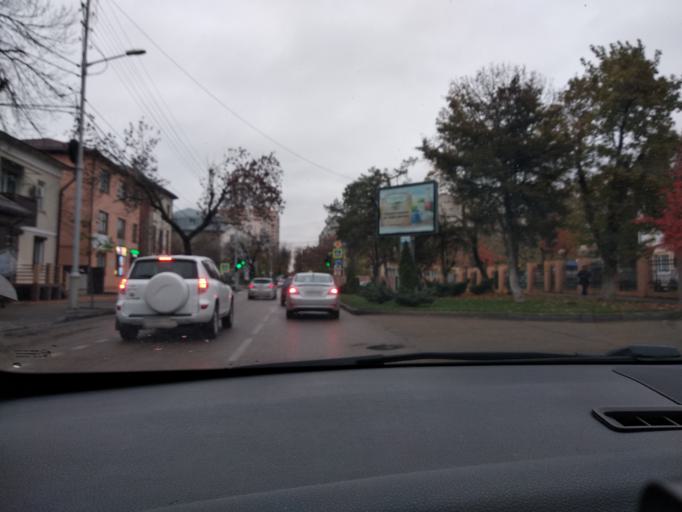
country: RU
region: Krasnodarskiy
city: Krasnodar
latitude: 45.0220
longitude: 38.9814
